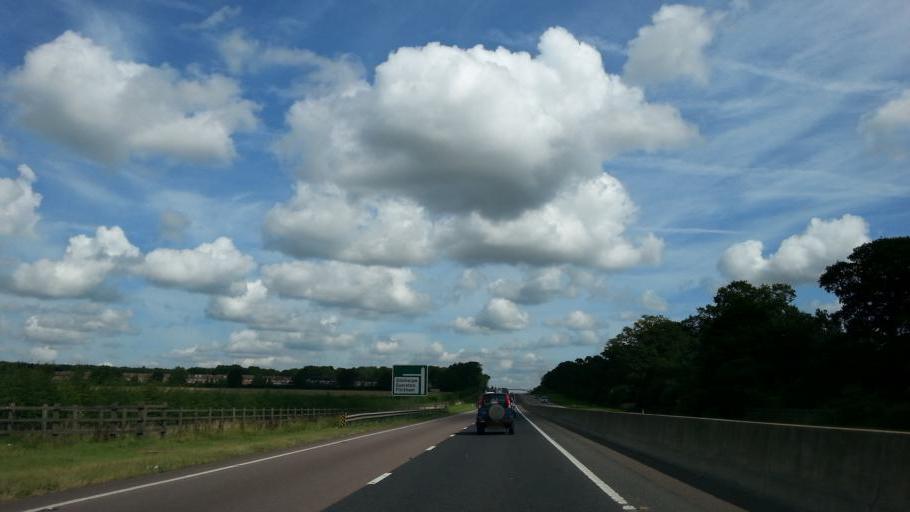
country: GB
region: England
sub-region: Nottinghamshire
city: East Bridgford
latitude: 53.0065
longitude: -0.9135
